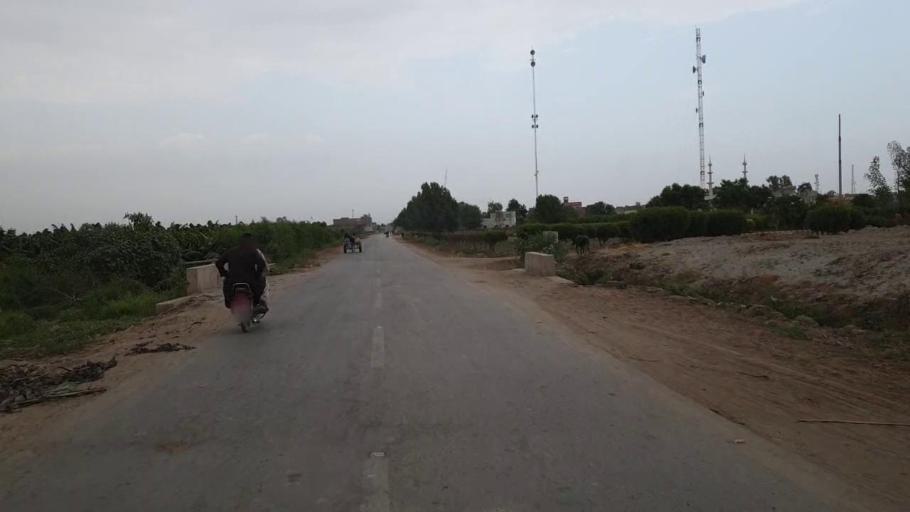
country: PK
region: Sindh
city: Bandhi
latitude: 26.5894
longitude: 68.2944
